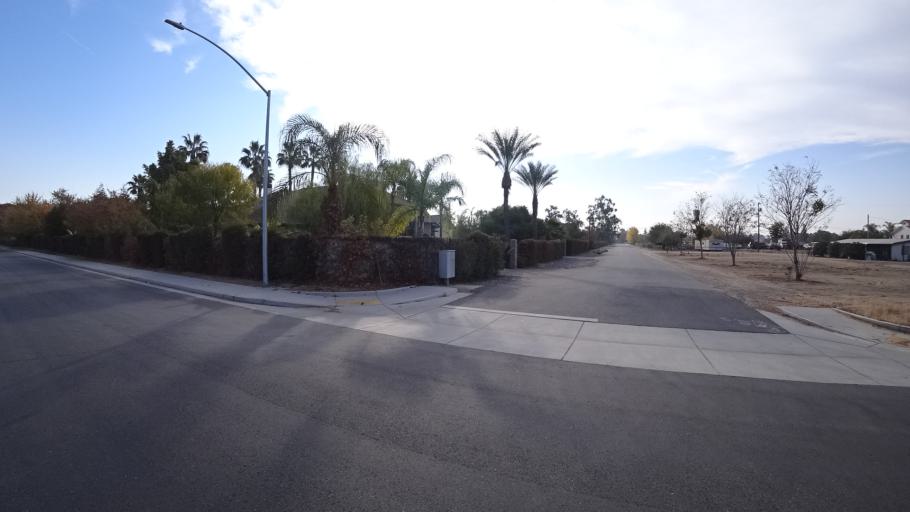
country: US
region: California
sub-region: Kern County
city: Rosedale
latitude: 35.3689
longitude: -119.1599
